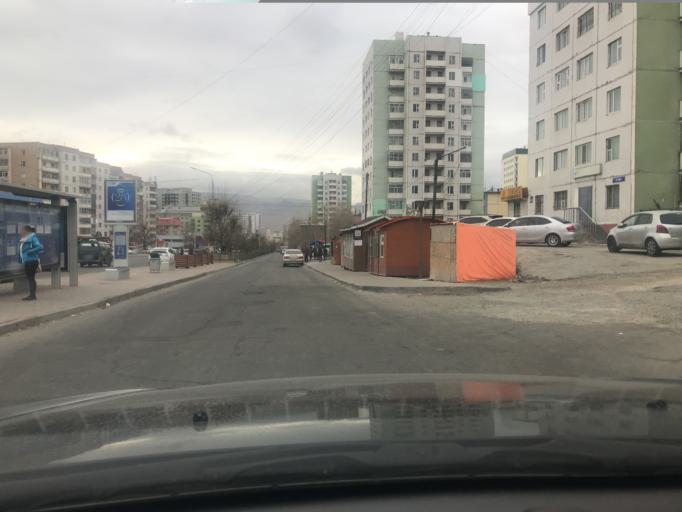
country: MN
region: Ulaanbaatar
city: Ulaanbaatar
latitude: 47.9238
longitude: 106.9417
